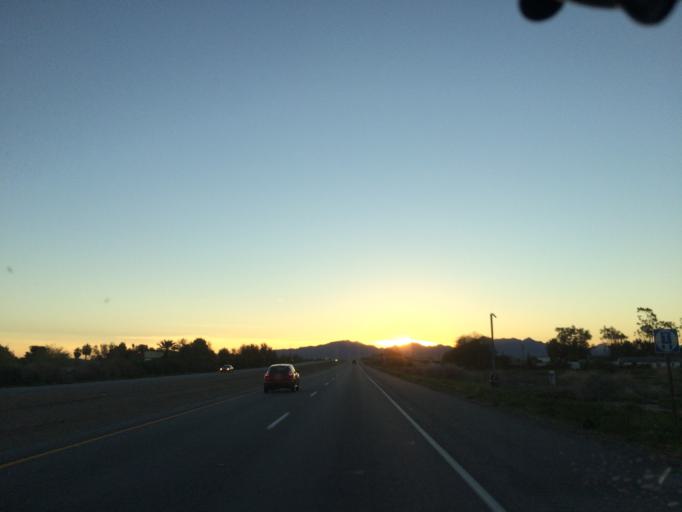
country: US
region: California
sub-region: Riverside County
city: Blythe
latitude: 33.6071
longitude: -114.5795
